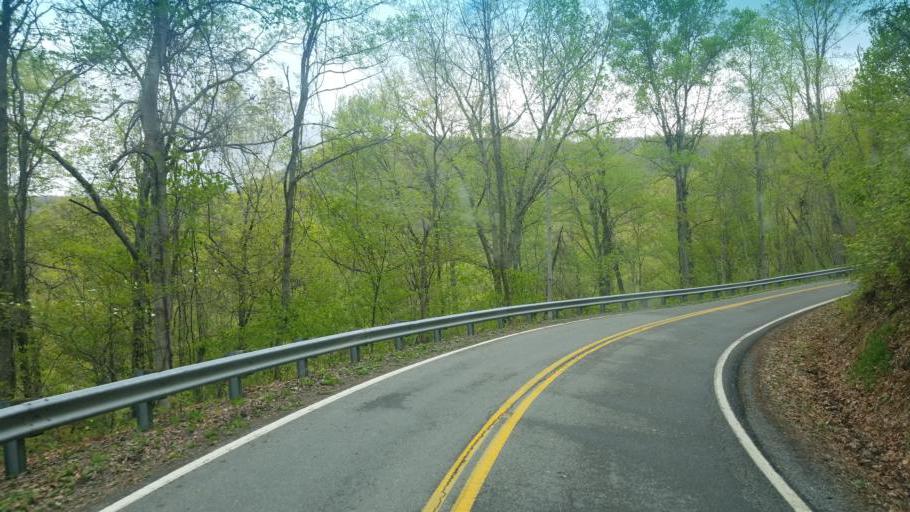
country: US
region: Virginia
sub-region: Tazewell County
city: Tazewell
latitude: 37.0120
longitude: -81.5206
